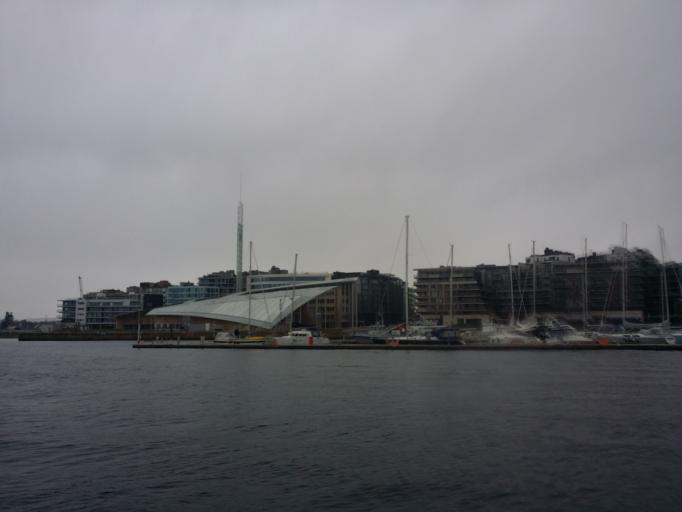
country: NO
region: Oslo
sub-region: Oslo
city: Oslo
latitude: 59.9063
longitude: 10.7264
